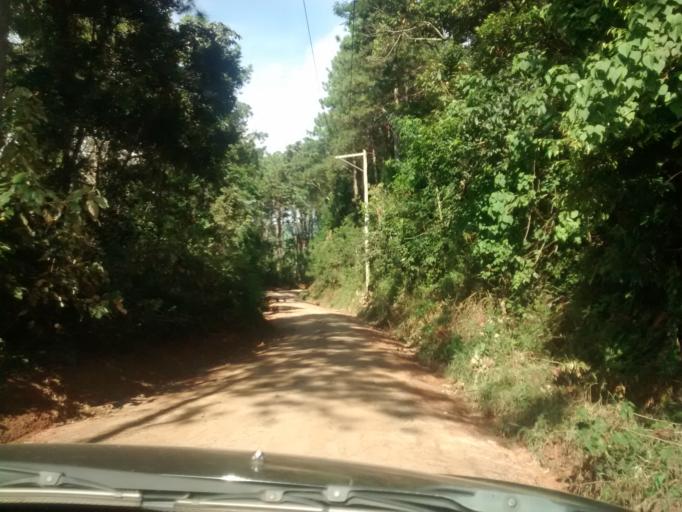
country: BR
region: Sao Paulo
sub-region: Campos Do Jordao
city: Campos do Jordao
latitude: -22.7392
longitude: -45.6657
